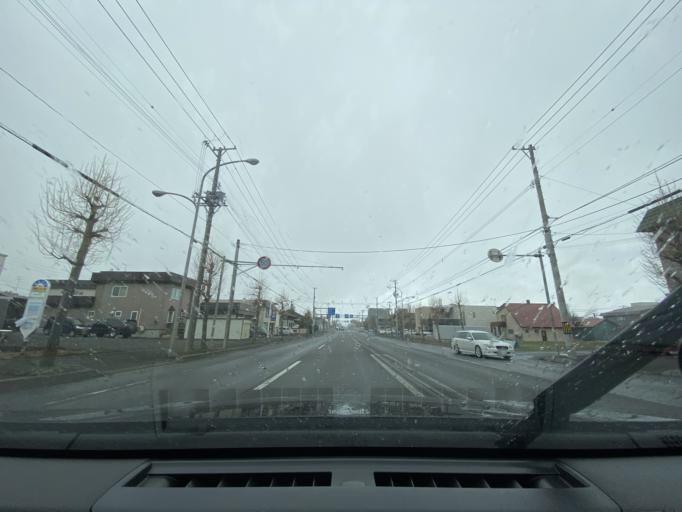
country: JP
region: Hokkaido
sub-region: Asahikawa-shi
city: Asahikawa
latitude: 43.8266
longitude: 142.4157
